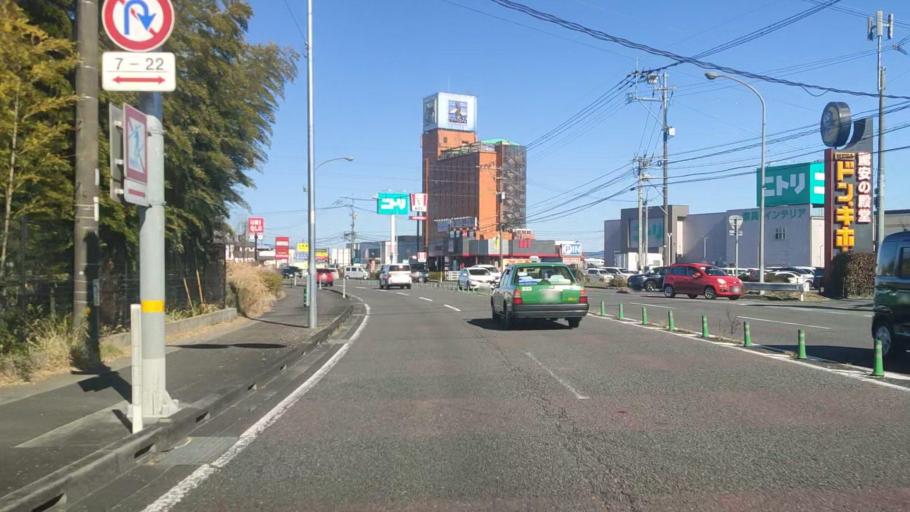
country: JP
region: Miyazaki
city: Miyakonojo
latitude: 31.7467
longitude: 131.0775
